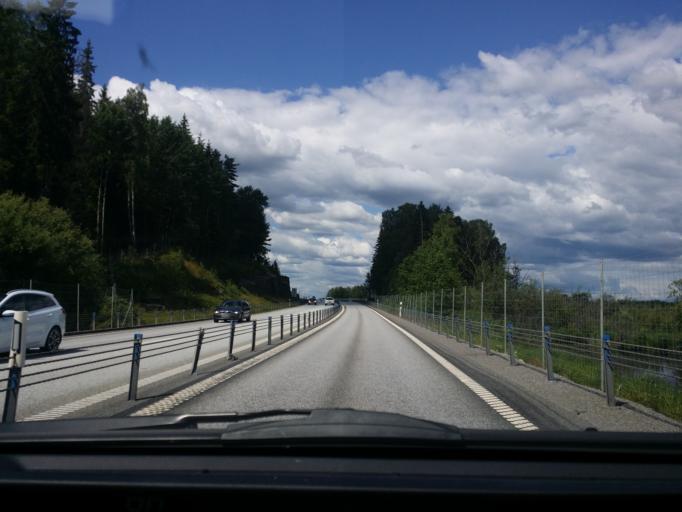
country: SE
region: OErebro
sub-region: Orebro Kommun
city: Hovsta
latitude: 59.3890
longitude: 15.2127
